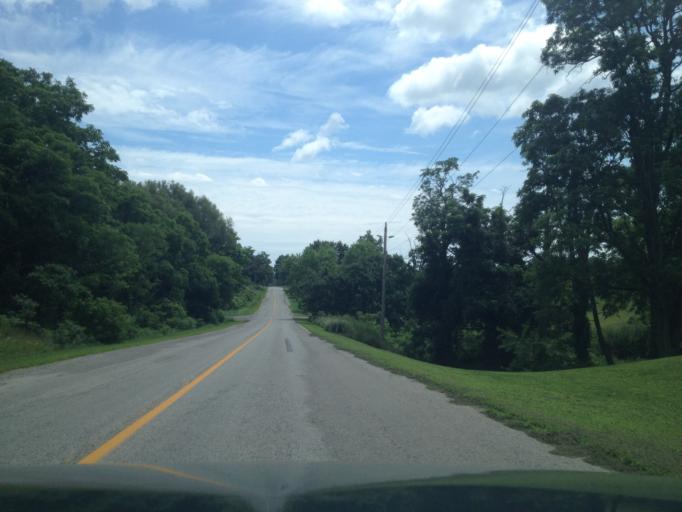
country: CA
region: Ontario
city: Norfolk County
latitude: 42.7819
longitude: -80.2991
